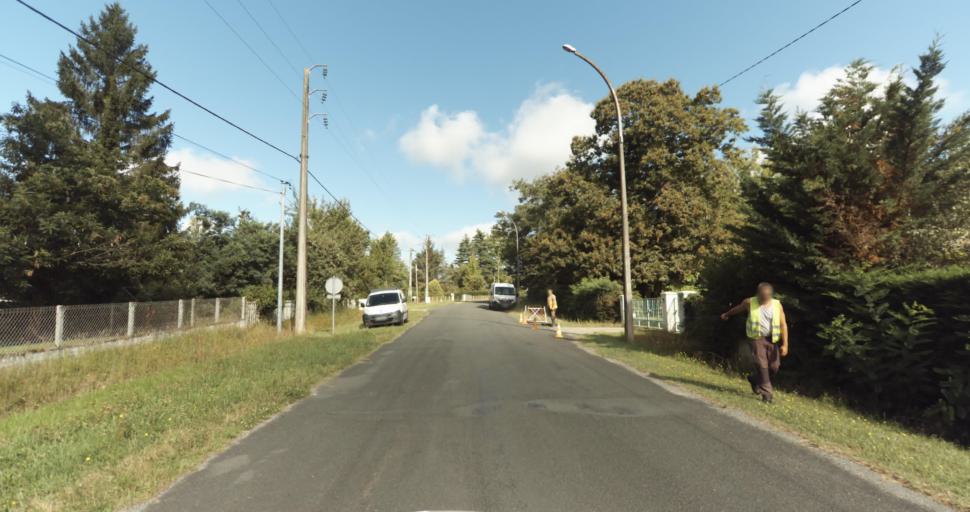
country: FR
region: Aquitaine
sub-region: Departement de la Gironde
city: Bazas
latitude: 44.4398
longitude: -0.2412
